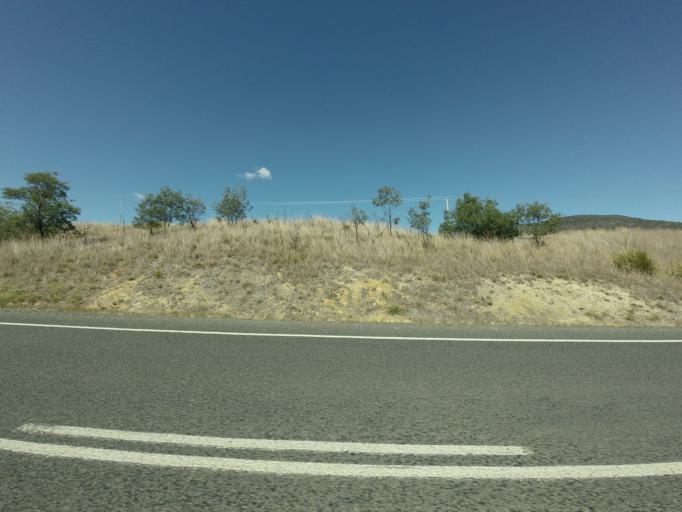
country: AU
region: Tasmania
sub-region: Break O'Day
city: St Helens
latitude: -41.7313
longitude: 147.8204
